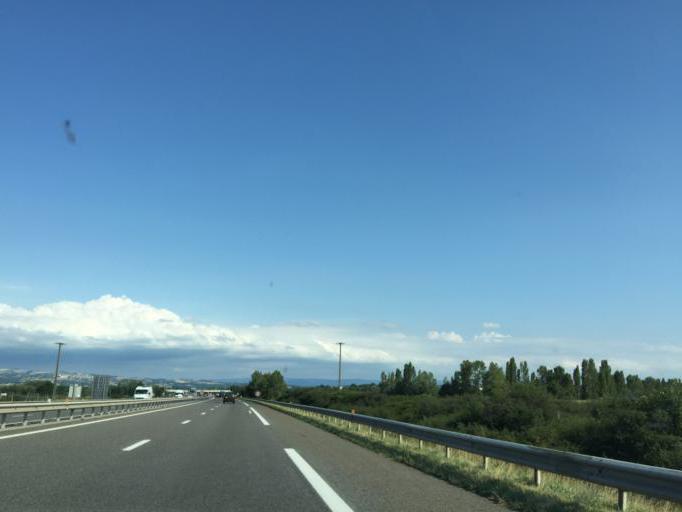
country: FR
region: Rhone-Alpes
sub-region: Departement de la Loire
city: Saint-Cyprien
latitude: 45.5643
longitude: 4.2334
